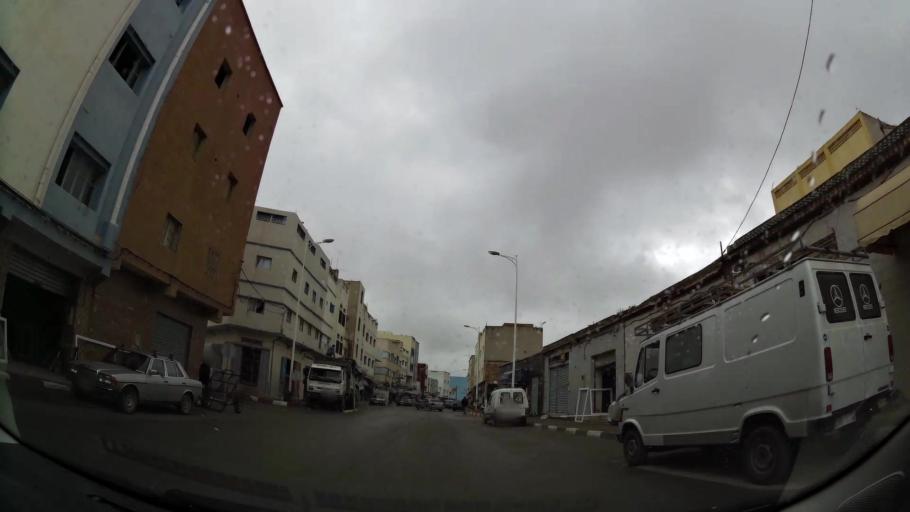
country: MA
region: Oriental
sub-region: Nador
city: Midar
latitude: 35.0467
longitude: -3.4527
